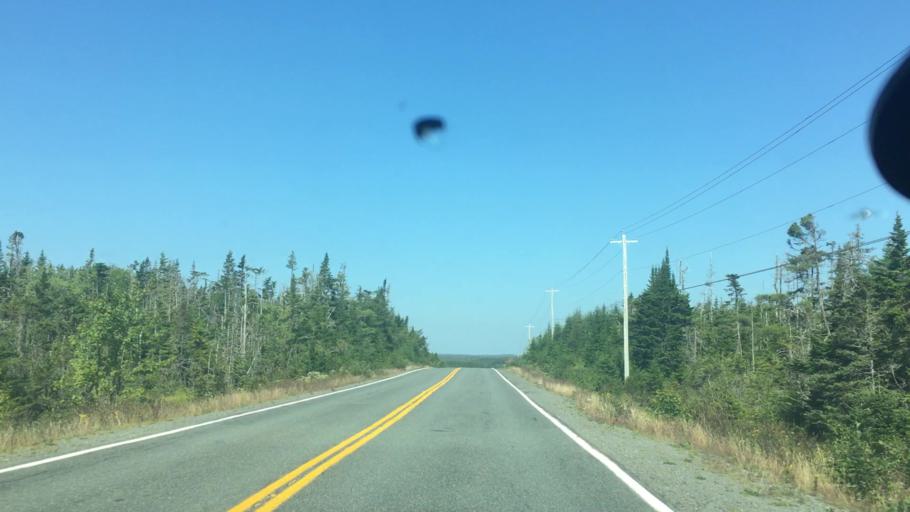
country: CA
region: Nova Scotia
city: Antigonish
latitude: 44.9909
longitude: -62.0961
